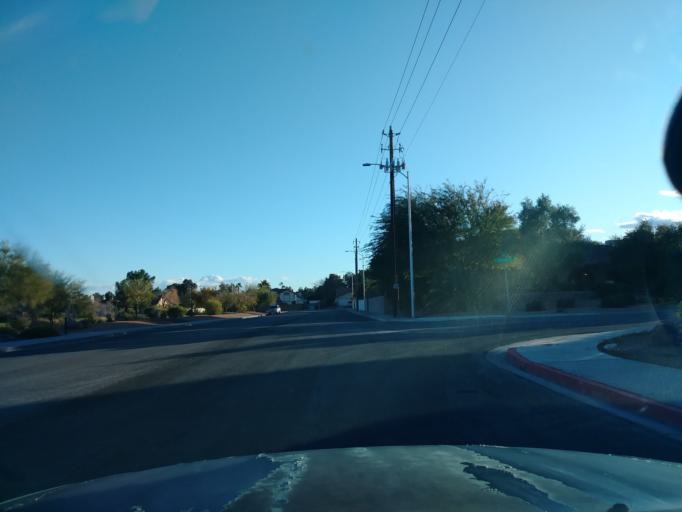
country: US
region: Nevada
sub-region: Clark County
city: Spring Valley
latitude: 36.1493
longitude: -115.2387
